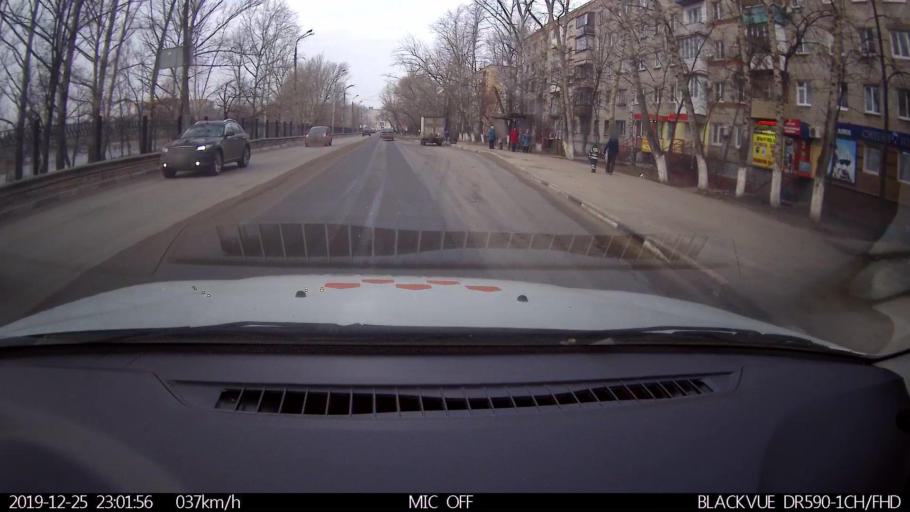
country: RU
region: Nizjnij Novgorod
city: Gorbatovka
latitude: 56.3543
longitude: 43.8387
